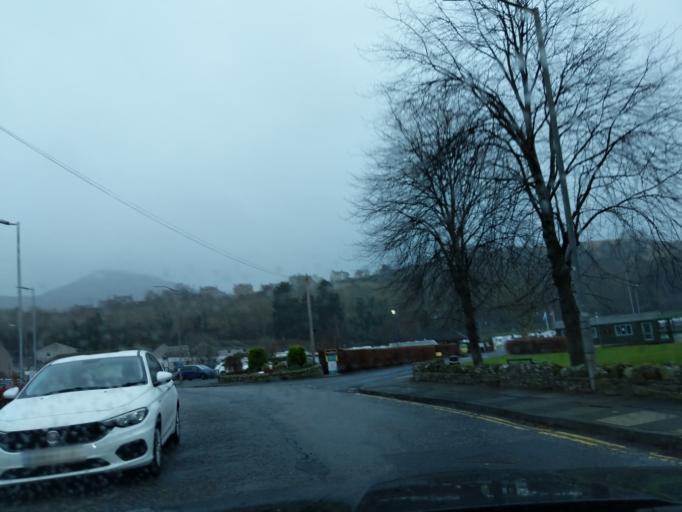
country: GB
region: Scotland
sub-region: The Scottish Borders
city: Melrose
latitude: 55.5987
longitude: -2.7234
